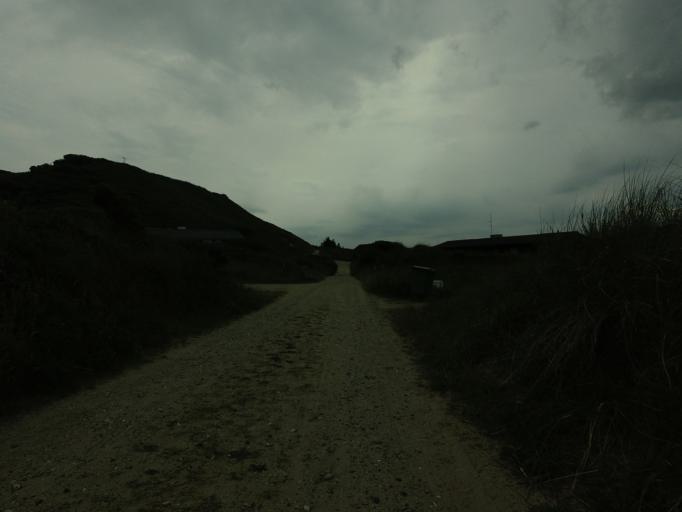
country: DK
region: North Denmark
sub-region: Jammerbugt Kommune
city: Pandrup
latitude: 57.3065
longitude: 9.6457
